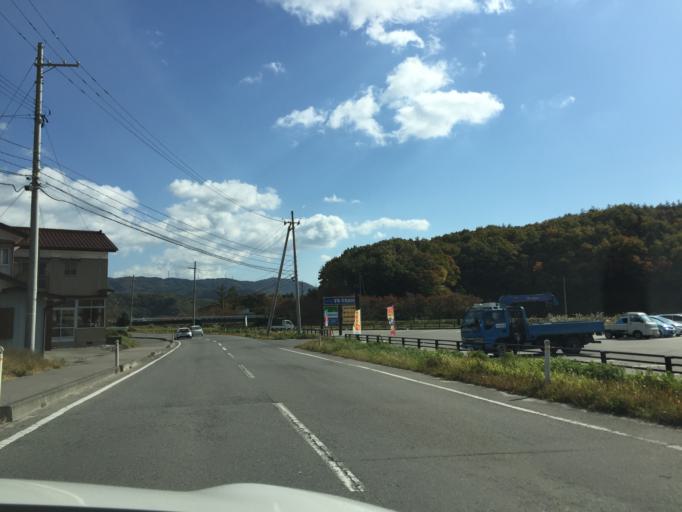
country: JP
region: Fukushima
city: Namie
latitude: 37.3296
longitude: 140.8218
